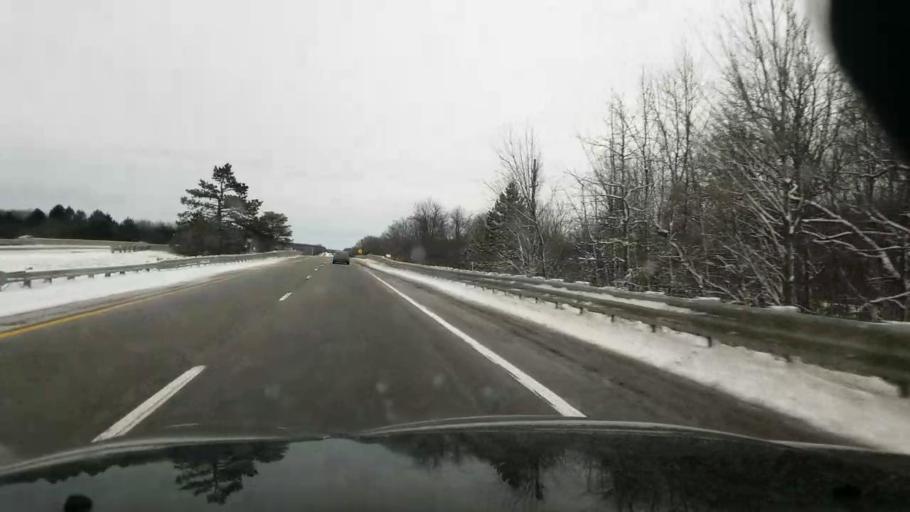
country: US
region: Michigan
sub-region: Jackson County
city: Jackson
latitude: 42.2701
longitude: -84.4774
